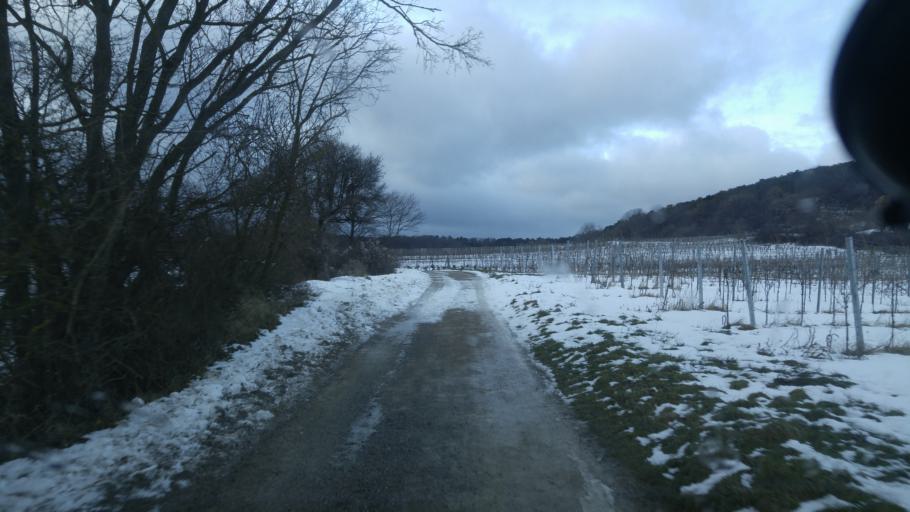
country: AT
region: Lower Austria
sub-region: Politischer Bezirk Baden
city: Hirtenberg
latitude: 47.9657
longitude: 16.1688
